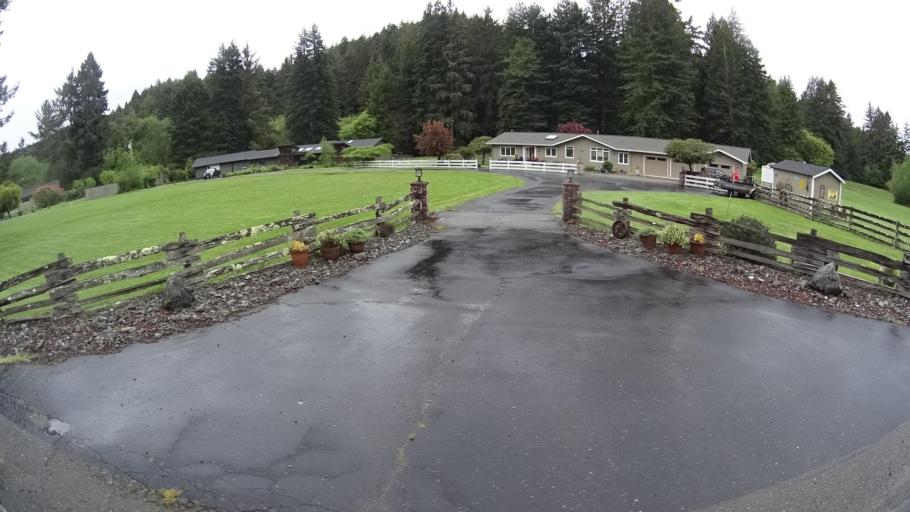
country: US
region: California
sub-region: Humboldt County
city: Bayside
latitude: 40.8313
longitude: -124.0410
